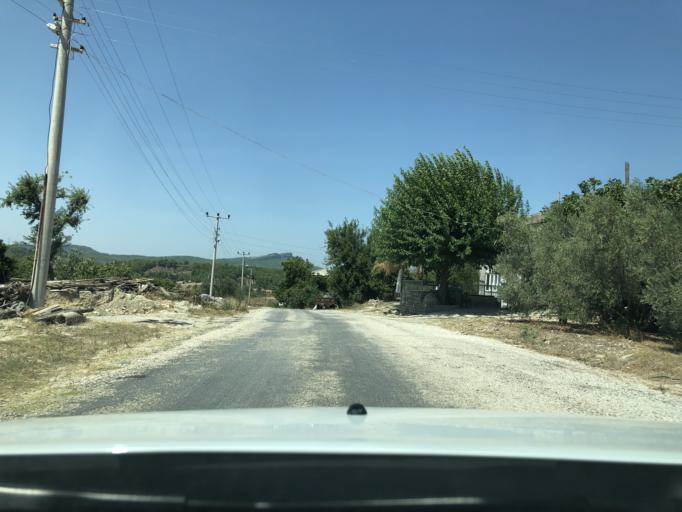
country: TR
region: Antalya
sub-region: Manavgat
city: Kizilagac
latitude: 36.8571
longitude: 31.5572
